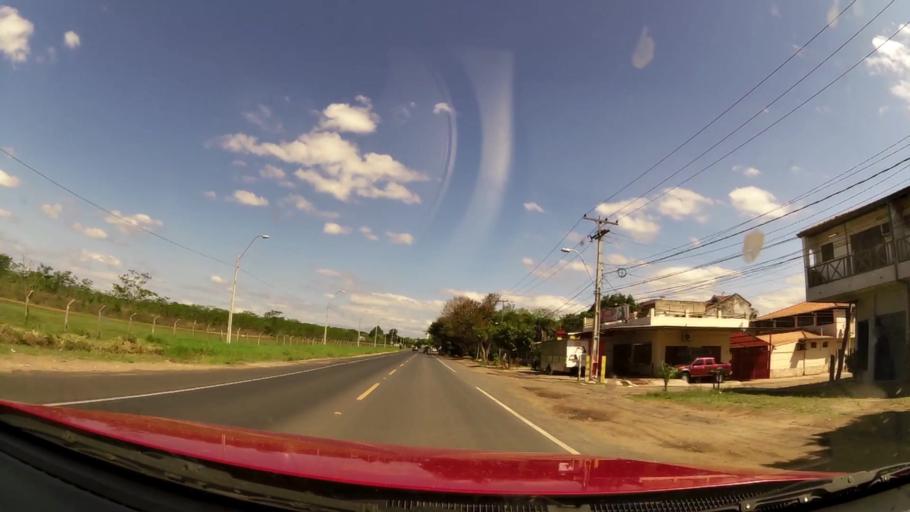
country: PY
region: Central
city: Fernando de la Mora
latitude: -25.2774
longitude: -57.5394
